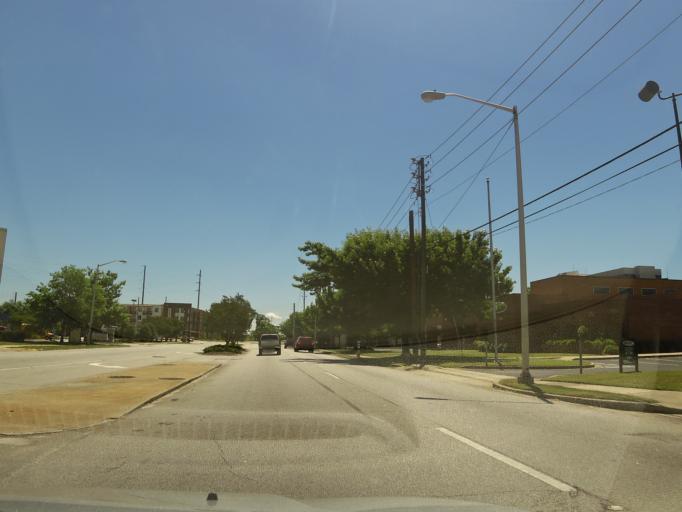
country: US
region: Georgia
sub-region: Richmond County
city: Augusta
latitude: 33.4742
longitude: -81.9844
